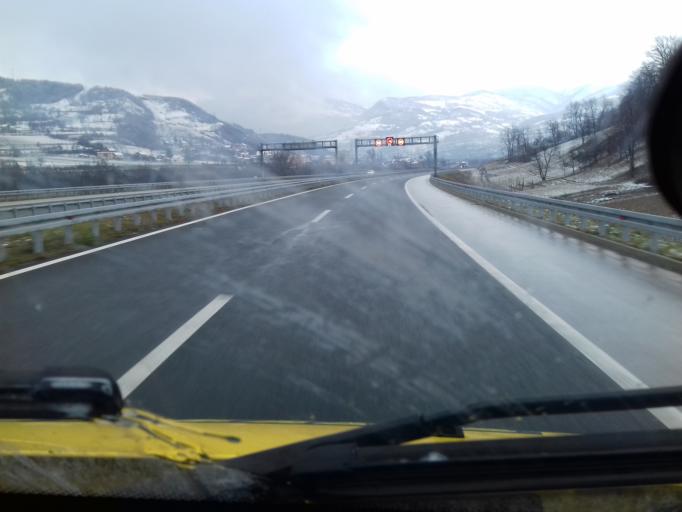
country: BA
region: Federation of Bosnia and Herzegovina
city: Zenica
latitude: 44.1592
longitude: 17.9660
